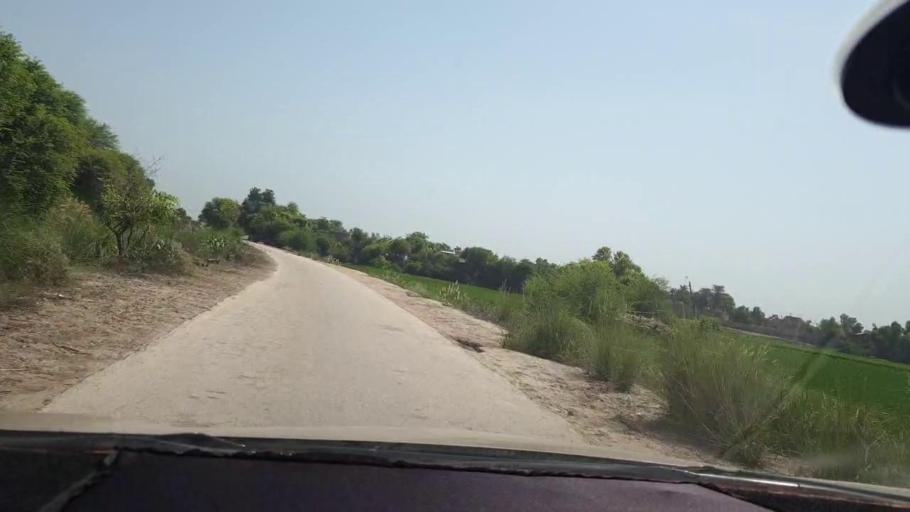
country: PK
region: Sindh
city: Kambar
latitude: 27.5097
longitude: 68.0121
